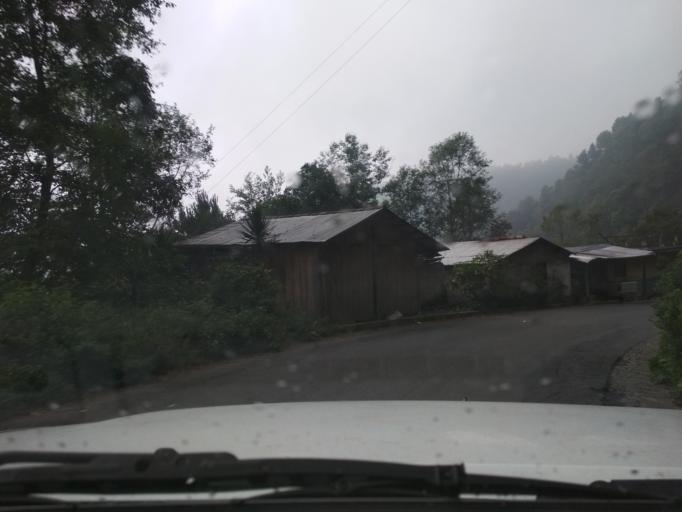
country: MX
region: Veracruz
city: La Perla
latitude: 18.9426
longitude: -97.1517
